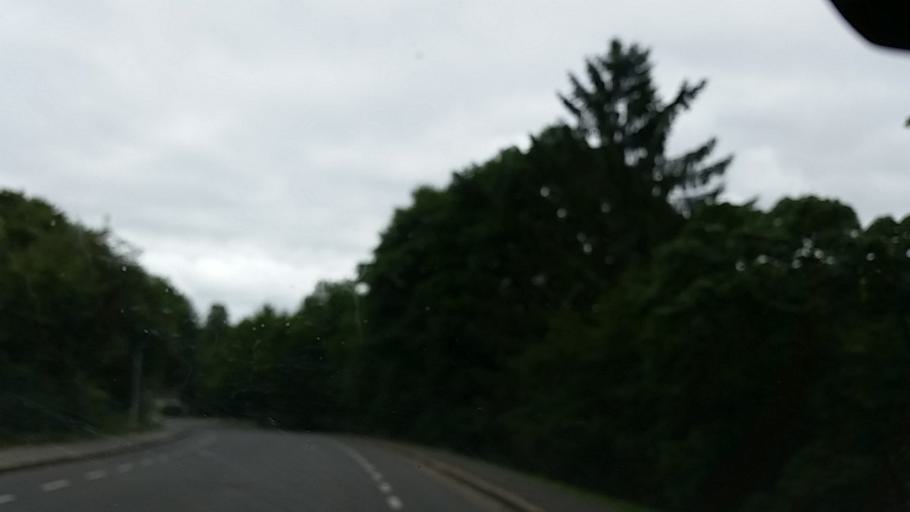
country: DE
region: Schleswig-Holstein
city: Busdorf
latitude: 54.5064
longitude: 9.5357
